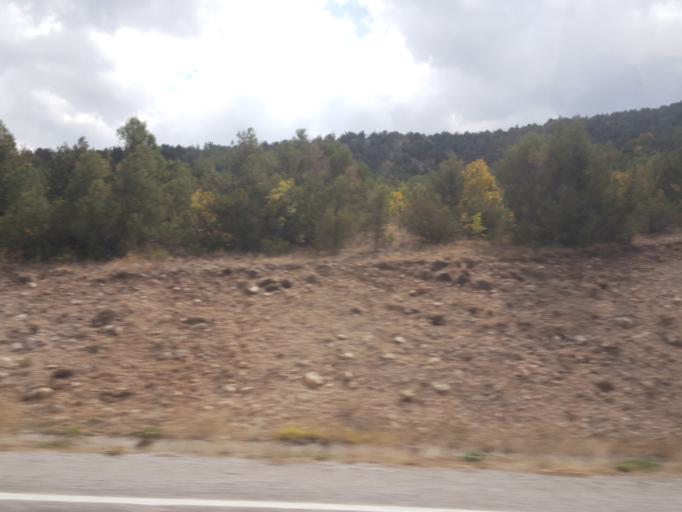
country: TR
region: Yozgat
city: Aydincik
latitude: 40.1862
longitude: 35.3974
